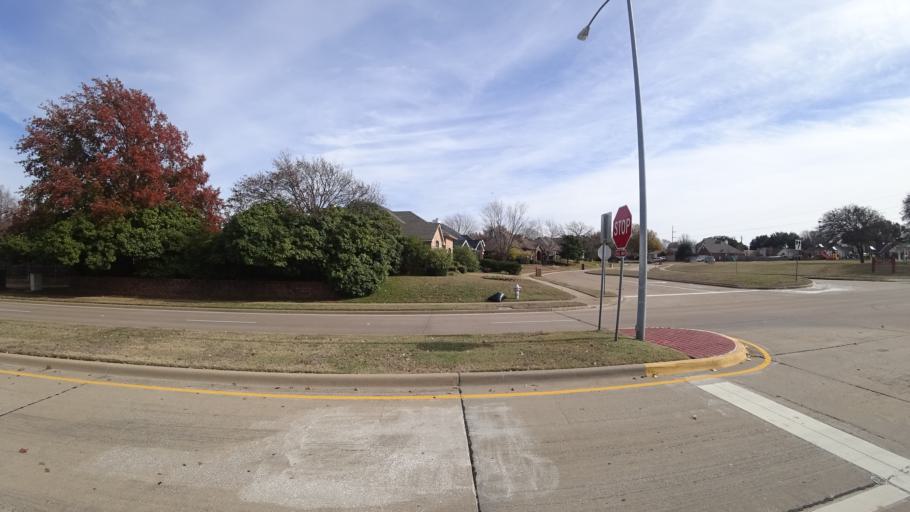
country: US
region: Texas
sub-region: Denton County
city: Highland Village
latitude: 33.0778
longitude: -97.0359
